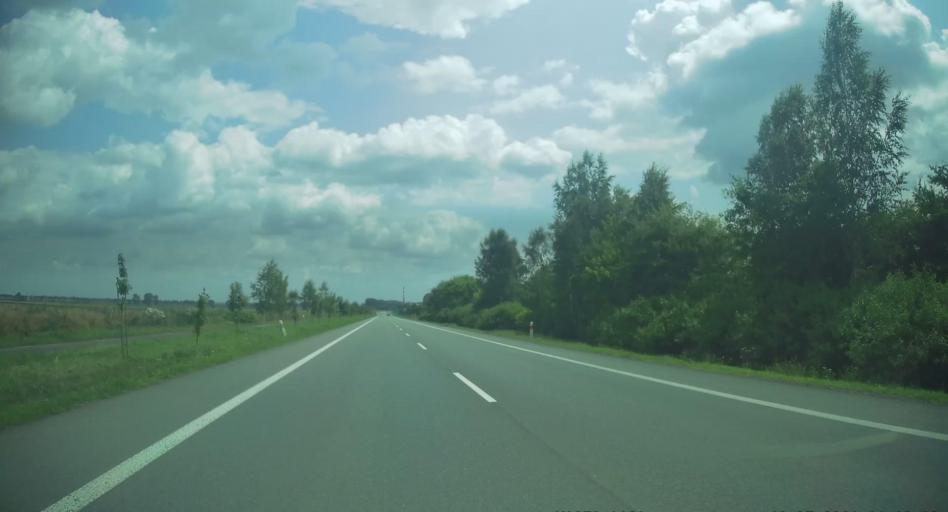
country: PL
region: Opole Voivodeship
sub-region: Powiat prudnicki
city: Prudnik
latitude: 50.3356
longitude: 17.5796
